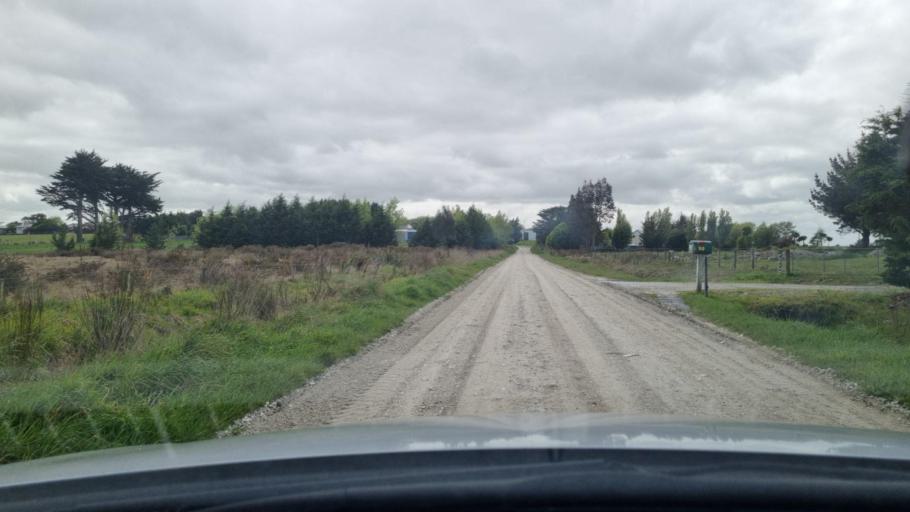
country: NZ
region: Southland
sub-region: Invercargill City
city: Invercargill
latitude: -46.4348
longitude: 168.3896
